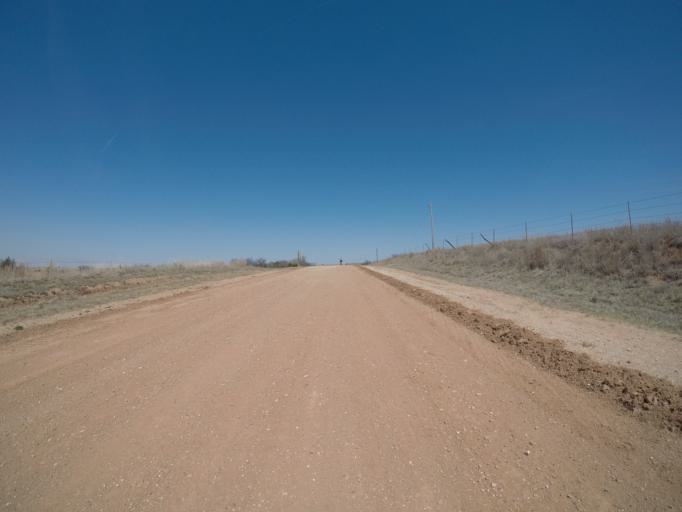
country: US
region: Kansas
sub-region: Pratt County
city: Pratt
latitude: 37.3937
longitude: -98.8320
